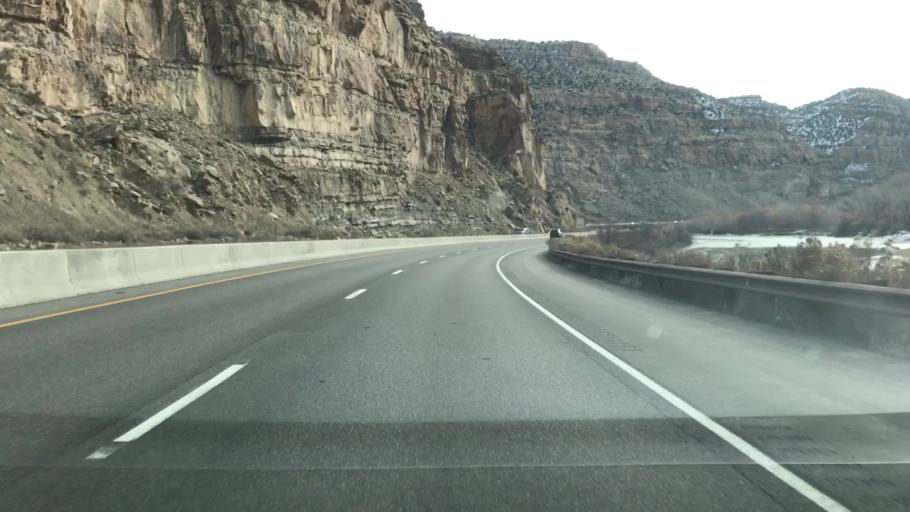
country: US
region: Colorado
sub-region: Mesa County
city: Palisade
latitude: 39.2298
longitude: -108.2664
